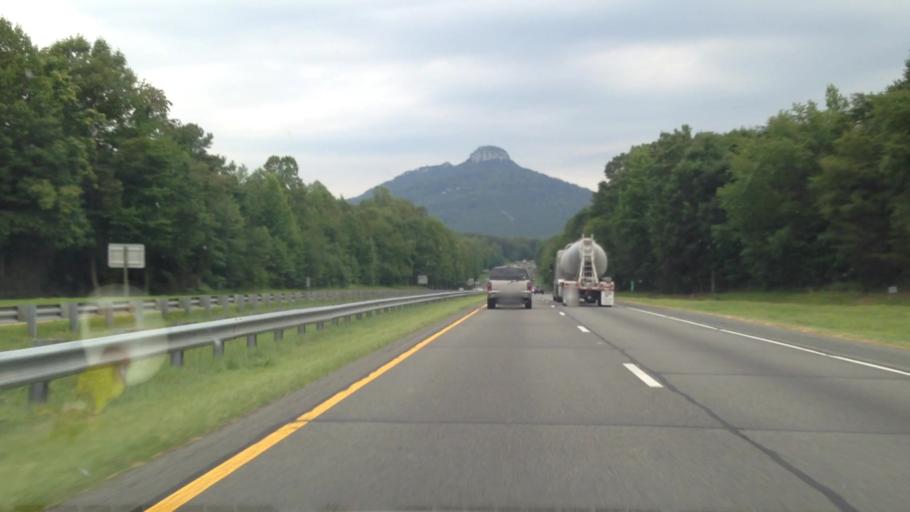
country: US
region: North Carolina
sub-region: Surry County
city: Pilot Mountain
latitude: 36.3181
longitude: -80.4397
